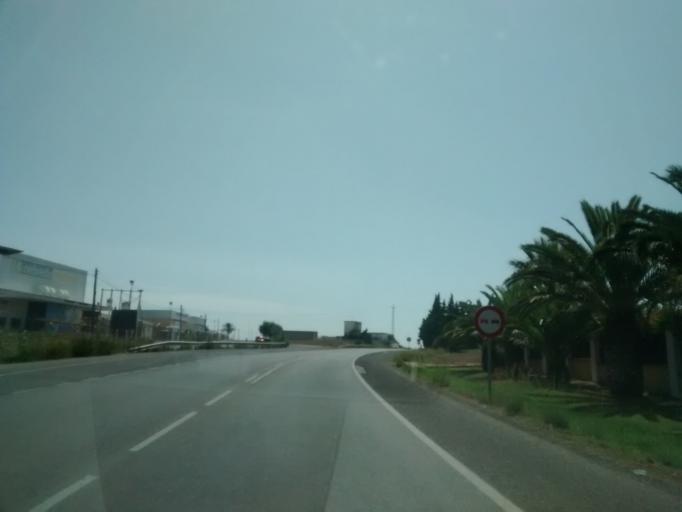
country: ES
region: Andalusia
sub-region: Provincia de Cadiz
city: Conil de la Frontera
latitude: 36.3075
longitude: -6.0810
